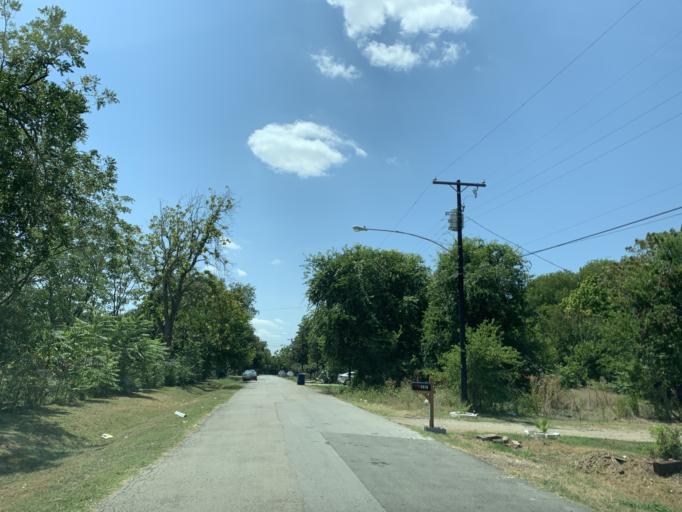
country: US
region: Texas
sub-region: Dallas County
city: Hutchins
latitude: 32.6865
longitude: -96.7801
